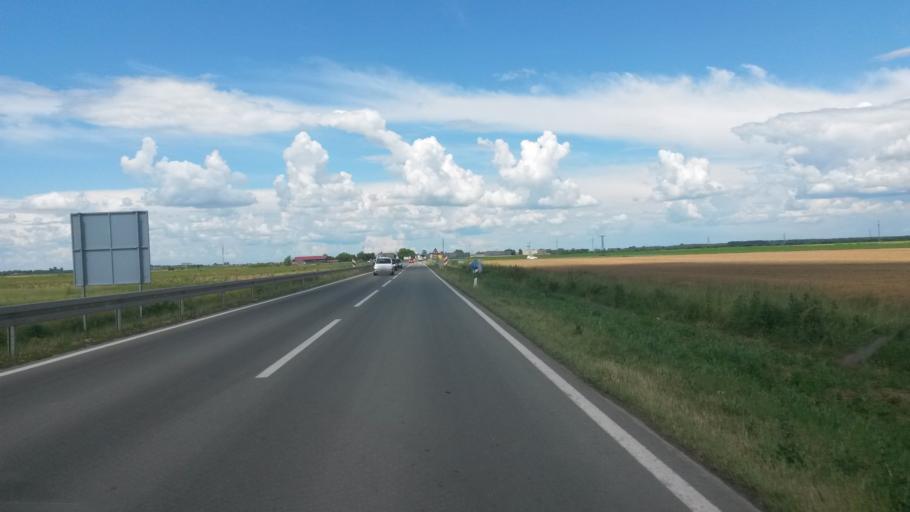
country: HR
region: Osjecko-Baranjska
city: Ovcara
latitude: 45.4871
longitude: 18.5468
